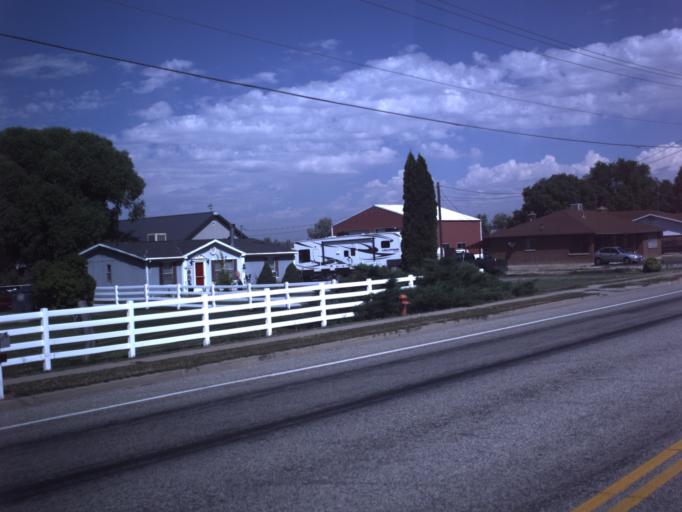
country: US
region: Utah
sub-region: Weber County
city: Farr West
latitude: 41.2911
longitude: -112.0278
